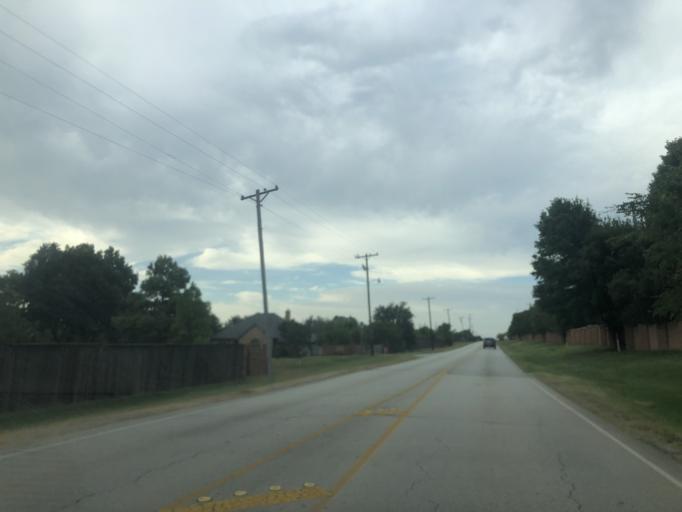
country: US
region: Texas
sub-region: Tarrant County
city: Southlake
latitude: 32.9485
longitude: -97.1511
